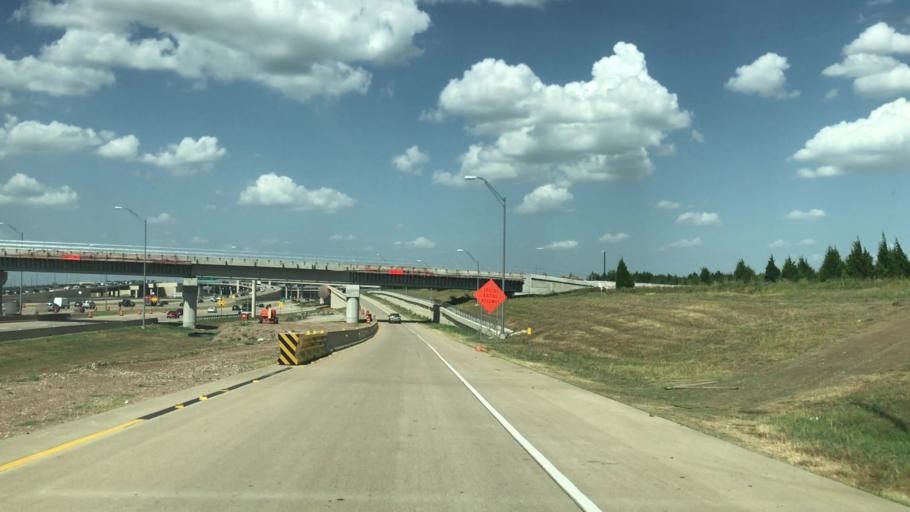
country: US
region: Texas
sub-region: Tarrant County
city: Grapevine
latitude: 32.9280
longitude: -97.0504
